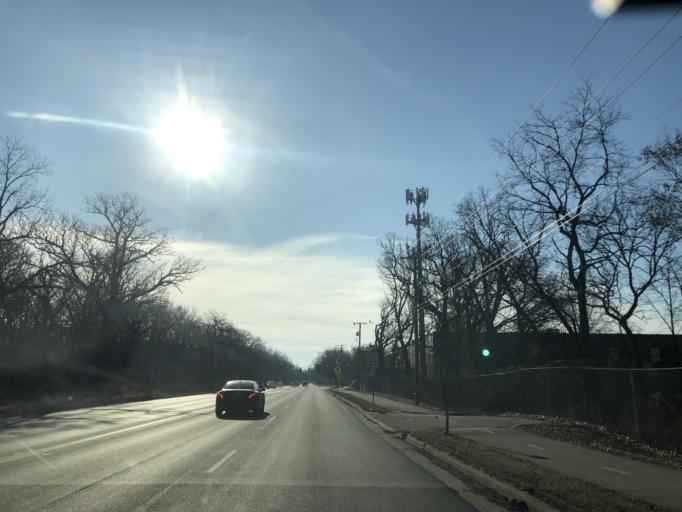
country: US
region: Illinois
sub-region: Cook County
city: Riverside
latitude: 41.8302
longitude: -87.8291
